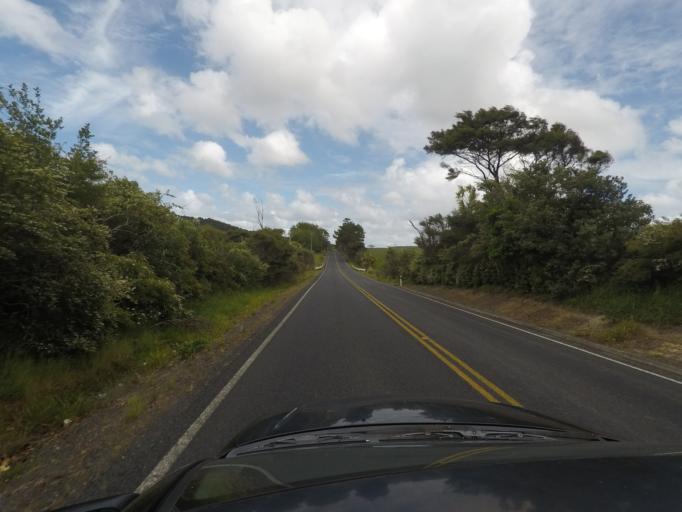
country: NZ
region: Auckland
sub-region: Auckland
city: Parakai
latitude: -36.6459
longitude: 174.5162
